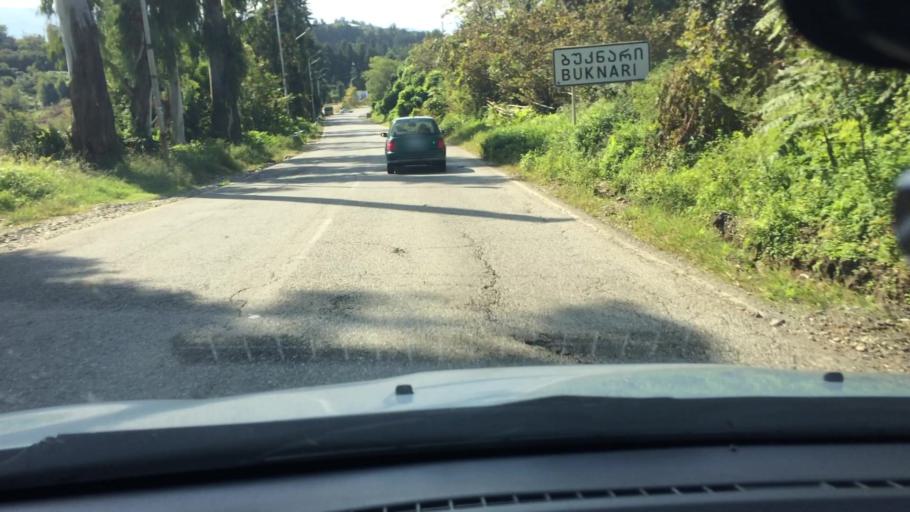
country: GE
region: Ajaria
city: Kobuleti
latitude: 41.7488
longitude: 41.7419
